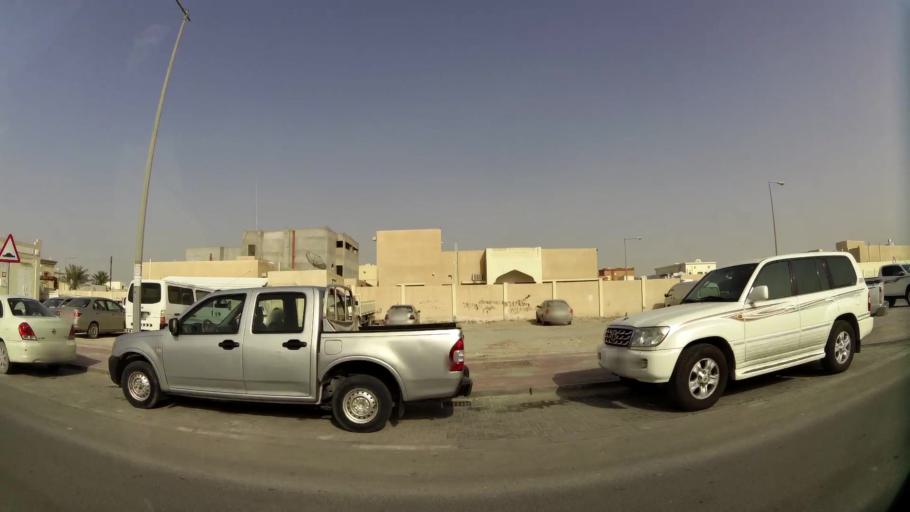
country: QA
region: Baladiyat ar Rayyan
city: Ar Rayyan
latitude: 25.2378
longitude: 51.4368
